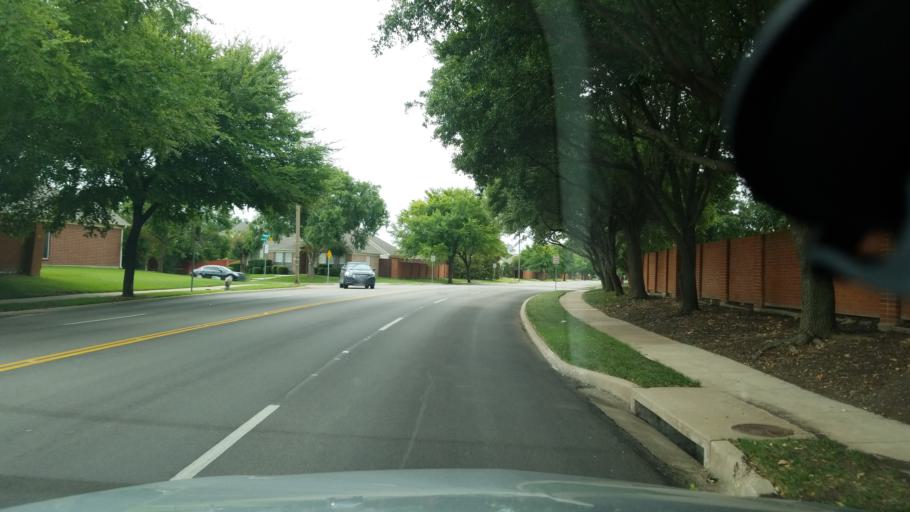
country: US
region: Texas
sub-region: Dallas County
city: Farmers Branch
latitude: 32.9444
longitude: -96.9449
